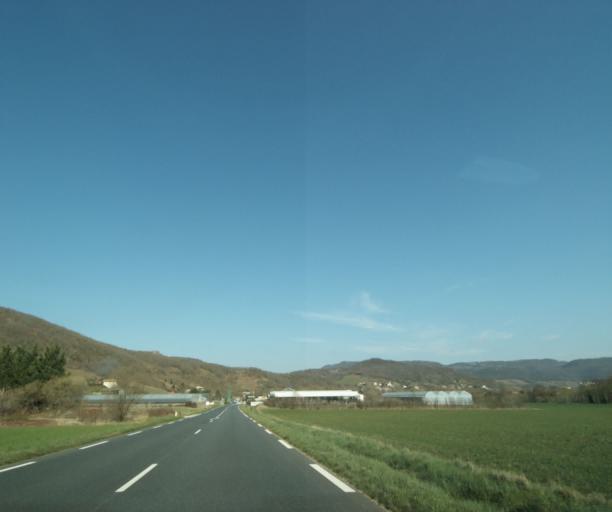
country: FR
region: Midi-Pyrenees
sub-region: Departement de l'Aveyron
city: Saint-Affrique
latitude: 43.9355
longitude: 2.8282
